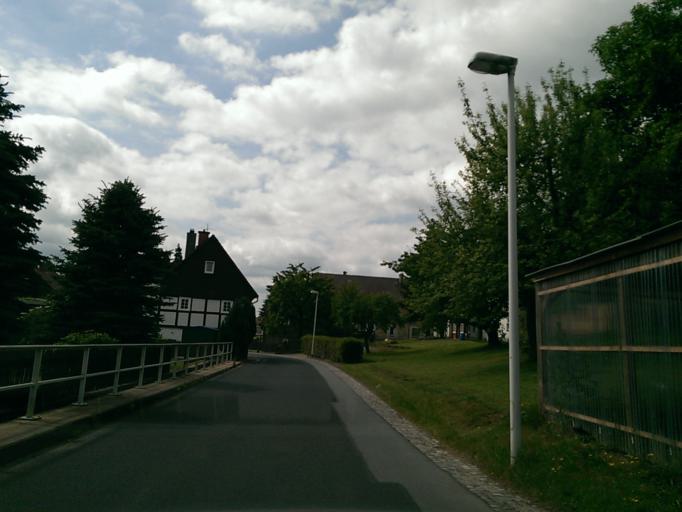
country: DE
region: Saxony
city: Mittelherwigsdorf
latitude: 50.9316
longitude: 14.7694
